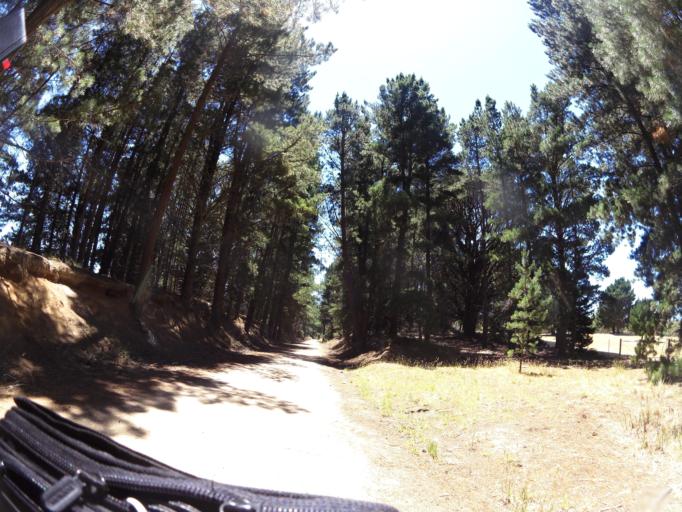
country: AU
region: Victoria
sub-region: Ballarat North
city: Delacombe
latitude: -37.5856
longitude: 143.7240
